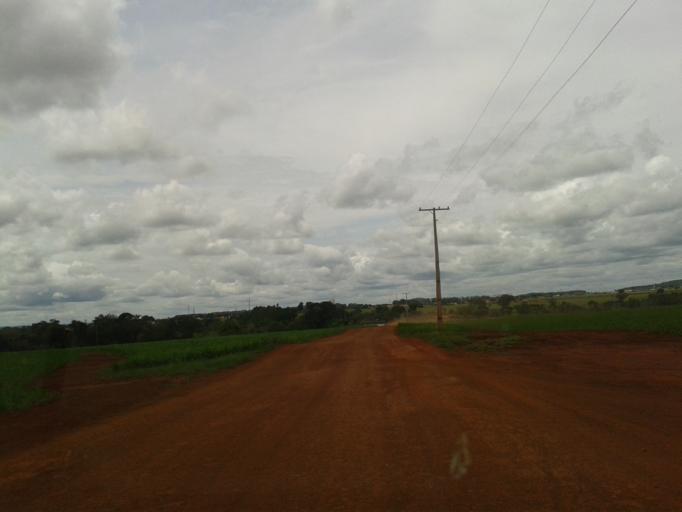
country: BR
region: Minas Gerais
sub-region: Centralina
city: Centralina
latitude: -18.5927
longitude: -49.2183
